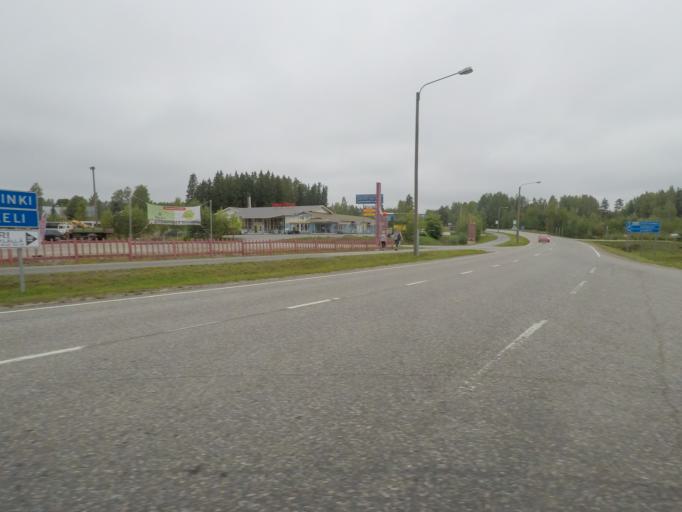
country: FI
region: Southern Savonia
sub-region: Mikkeli
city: Pertunmaa
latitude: 61.4225
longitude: 26.4343
